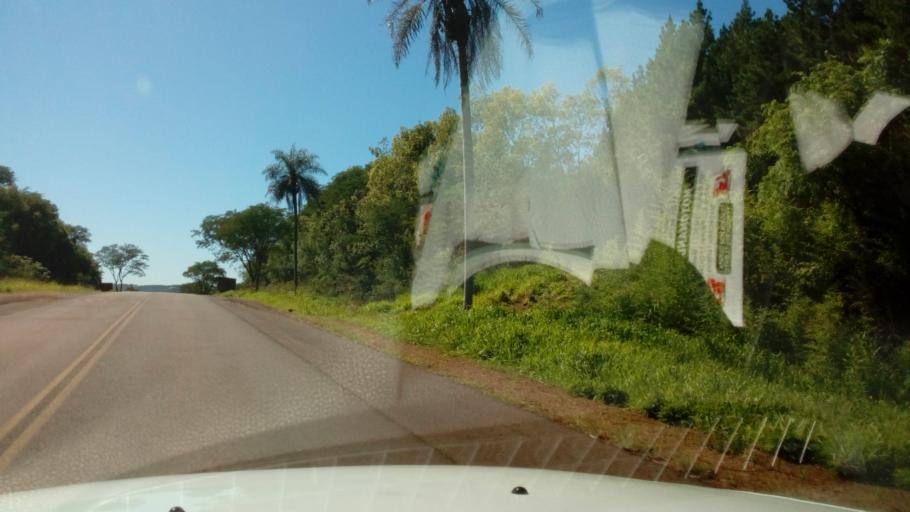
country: AR
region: Misiones
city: Almafuerte
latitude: -27.5593
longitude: -55.4160
